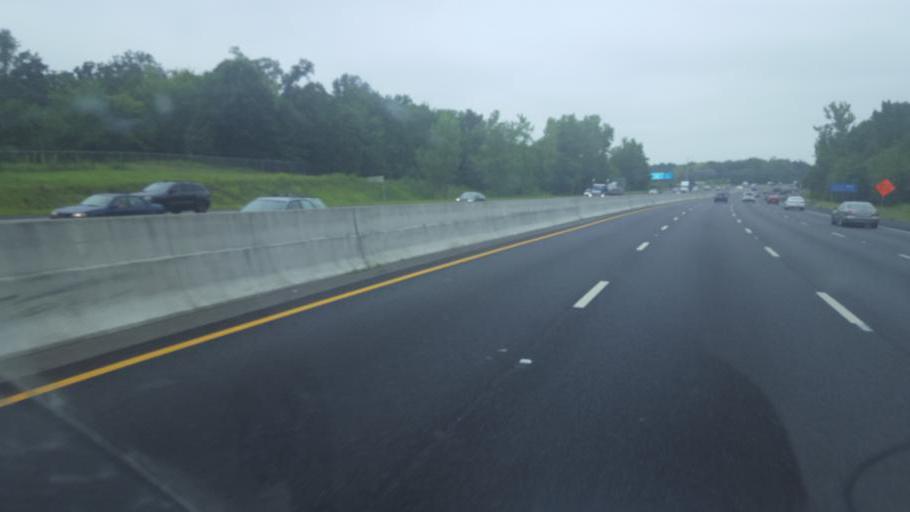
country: US
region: North Carolina
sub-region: Mecklenburg County
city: Pineville
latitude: 35.1009
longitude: -80.9316
